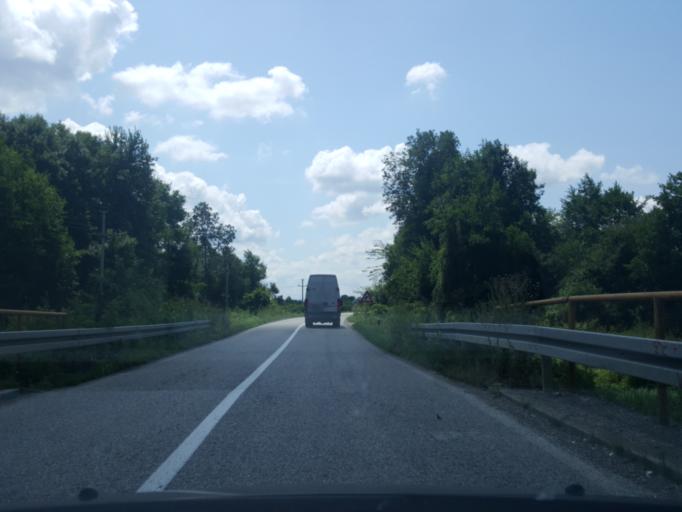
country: RS
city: Glusci
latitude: 44.9034
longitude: 19.5467
